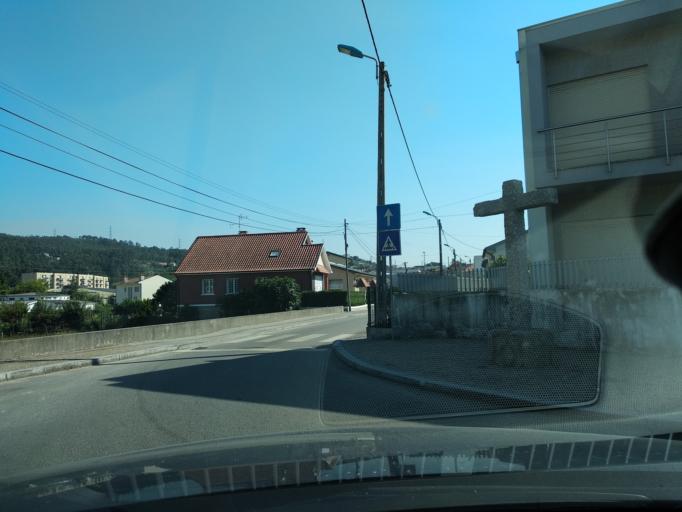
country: PT
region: Porto
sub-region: Paredes
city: Rebordosa
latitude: 41.2230
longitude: -8.4145
